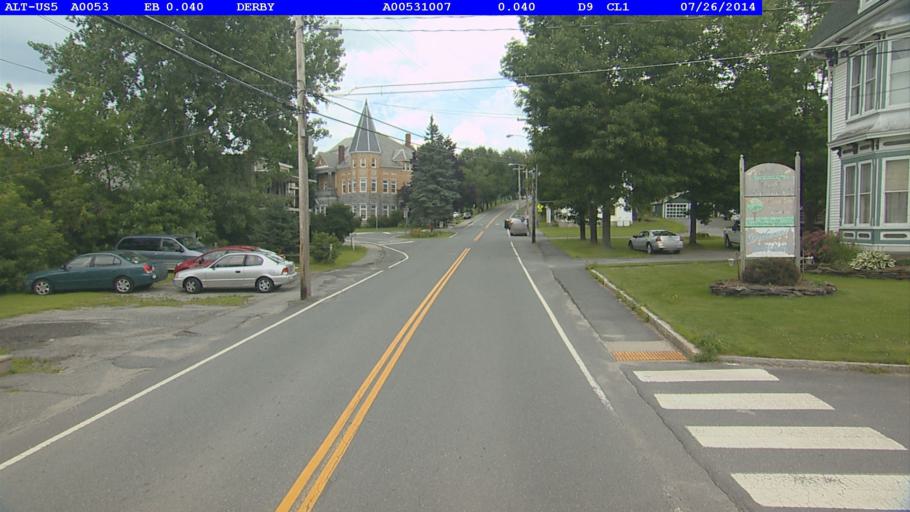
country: US
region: Vermont
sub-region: Orleans County
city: Newport
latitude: 45.0054
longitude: -72.0990
